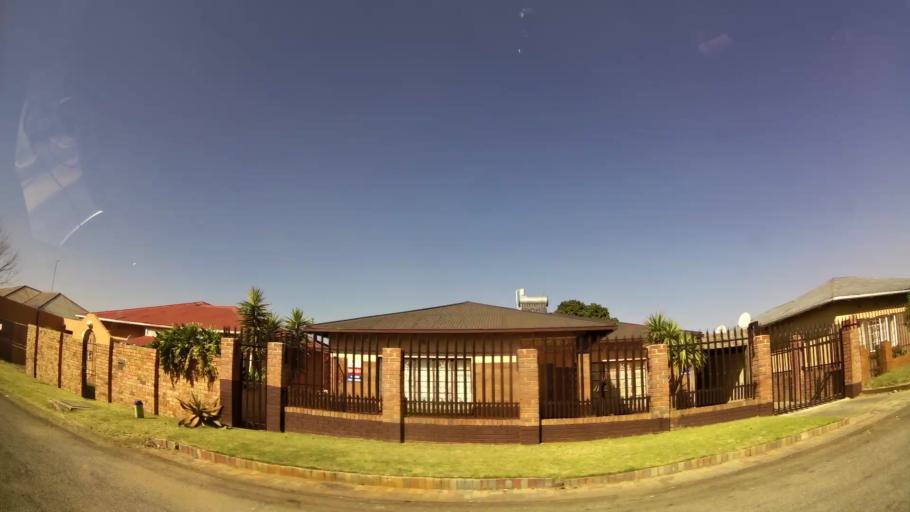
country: ZA
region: Gauteng
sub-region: City of Johannesburg Metropolitan Municipality
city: Roodepoort
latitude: -26.1754
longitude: 27.9588
